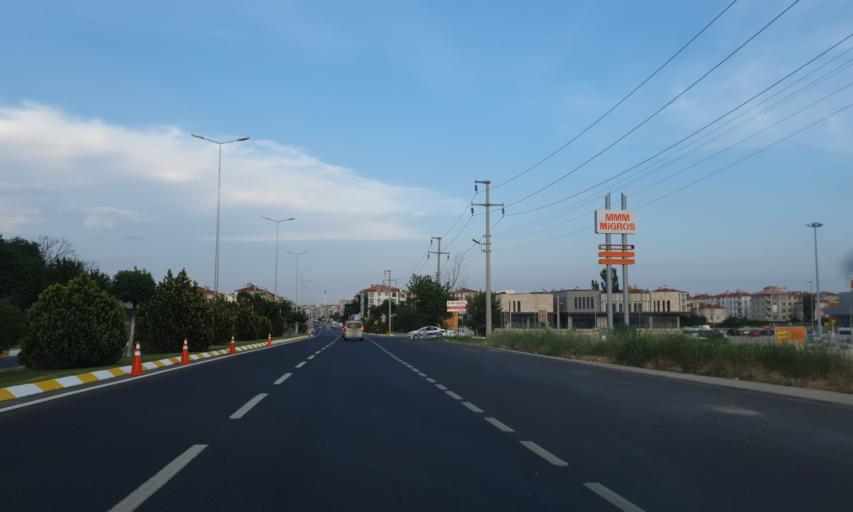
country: TR
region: Kirklareli
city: Luleburgaz
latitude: 41.4041
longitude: 27.3439
